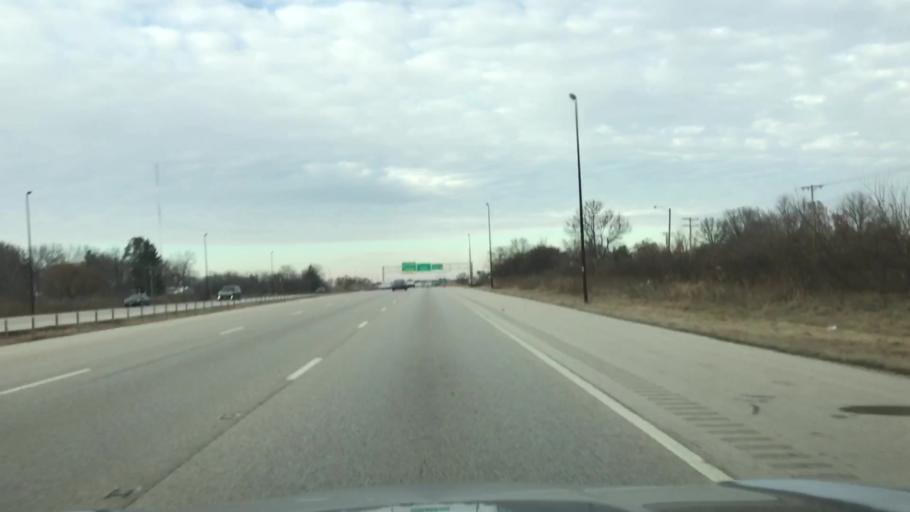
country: US
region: Illinois
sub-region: Sangamon County
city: Southern View
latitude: 39.7066
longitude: -89.6435
